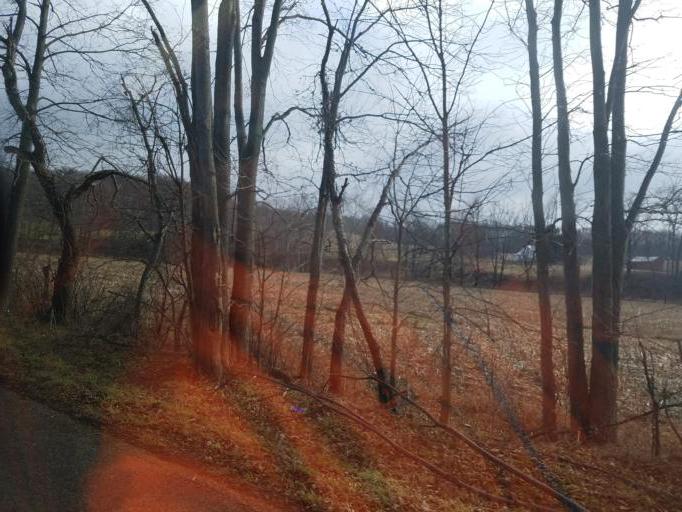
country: US
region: Ohio
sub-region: Richland County
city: Lexington
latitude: 40.6668
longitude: -82.5459
